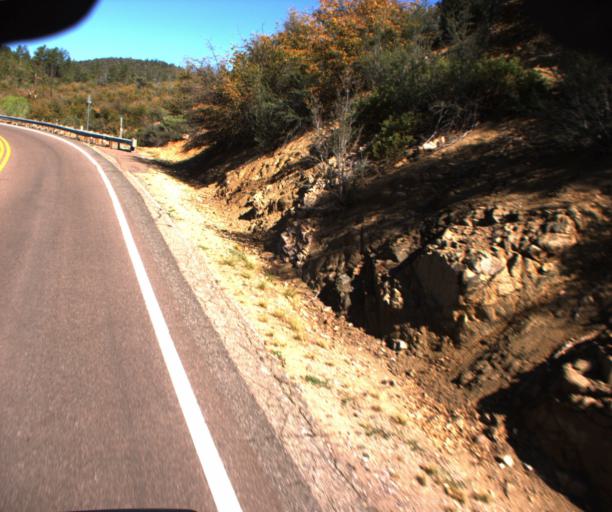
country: US
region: Arizona
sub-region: Yavapai County
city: Prescott
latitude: 34.4939
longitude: -112.4982
